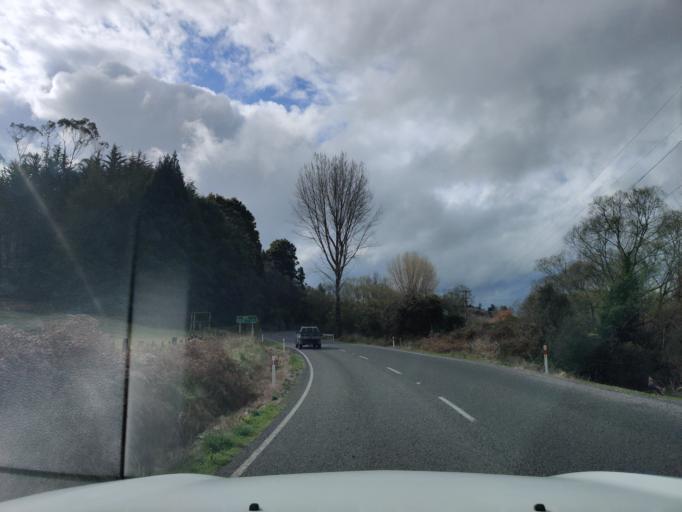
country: NZ
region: Manawatu-Wanganui
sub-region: Ruapehu District
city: Waiouru
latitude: -39.4246
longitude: 175.2818
